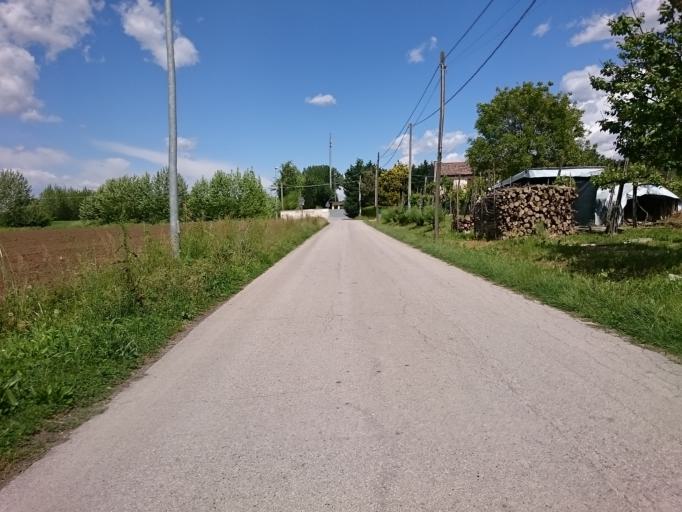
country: IT
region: Veneto
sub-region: Provincia di Padova
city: Terradura
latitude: 45.3418
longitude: 11.8195
